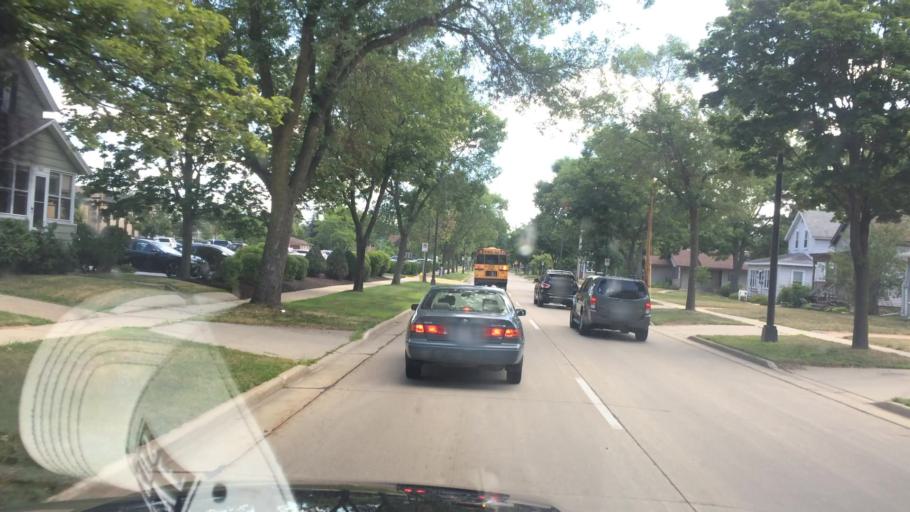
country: US
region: Wisconsin
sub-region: Portage County
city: Stevens Point
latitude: 44.5224
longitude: -89.5640
